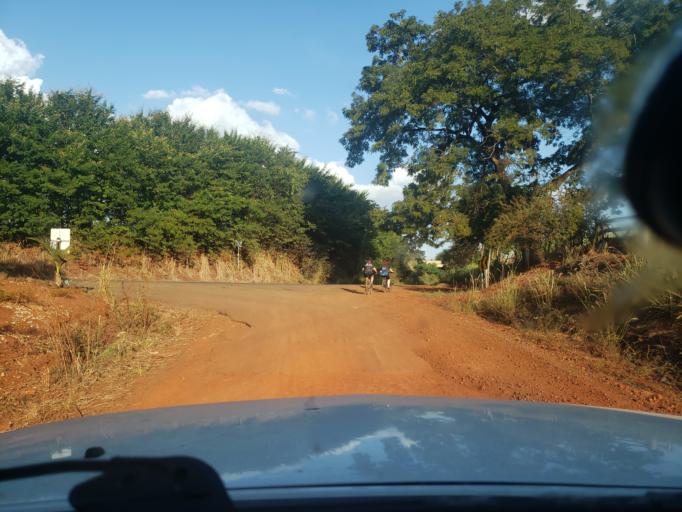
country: BR
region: Sao Paulo
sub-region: Mogi-Mirim
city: Mogi Mirim
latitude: -22.4600
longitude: -46.9357
